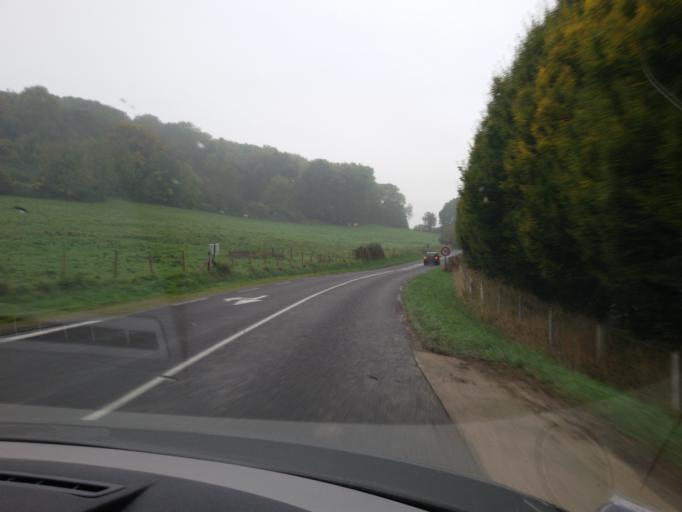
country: FR
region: Lower Normandy
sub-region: Departement du Calvados
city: Ablon
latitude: 49.4242
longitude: 0.3368
